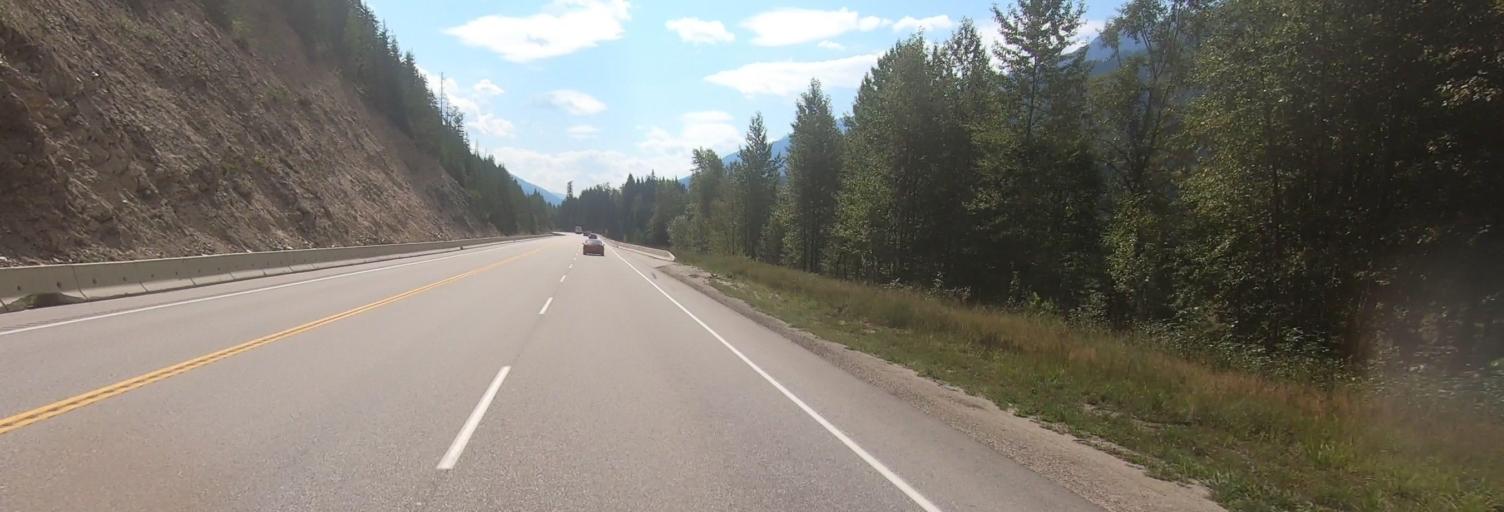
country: CA
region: British Columbia
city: Golden
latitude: 51.4013
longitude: -117.4636
